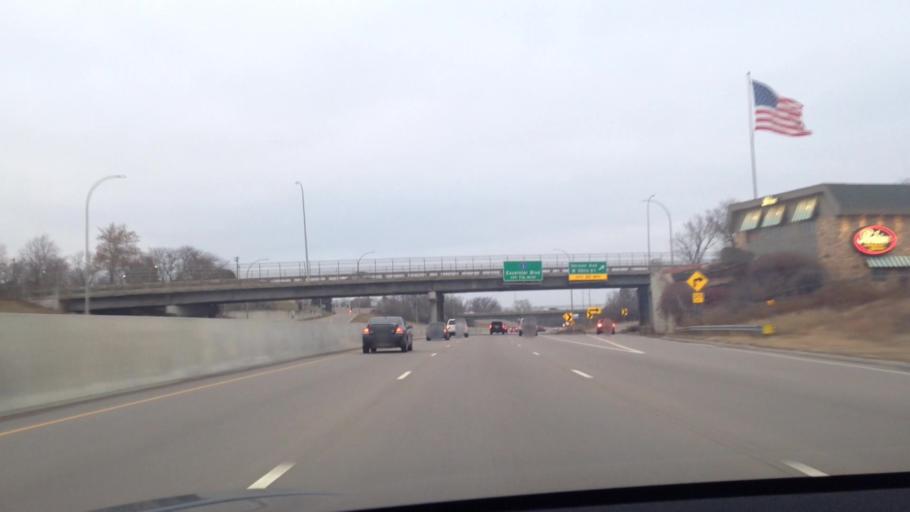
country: US
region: Minnesota
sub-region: Hennepin County
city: Edina
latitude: 44.9092
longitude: -93.3505
